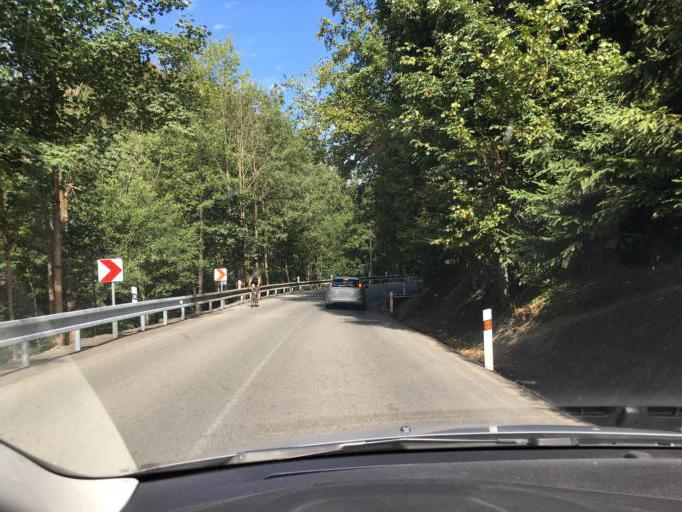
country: CZ
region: Liberecky
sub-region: Okres Semily
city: Ponikla
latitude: 50.6435
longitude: 15.4617
